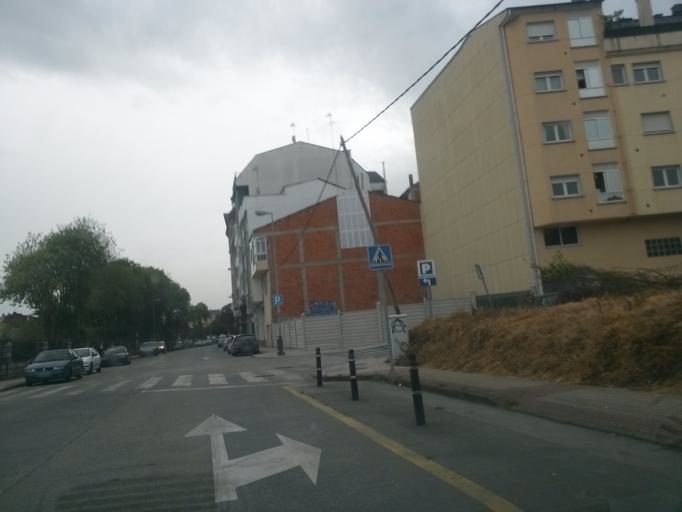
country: ES
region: Galicia
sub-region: Provincia de Lugo
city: Lugo
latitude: 43.0251
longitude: -7.5629
